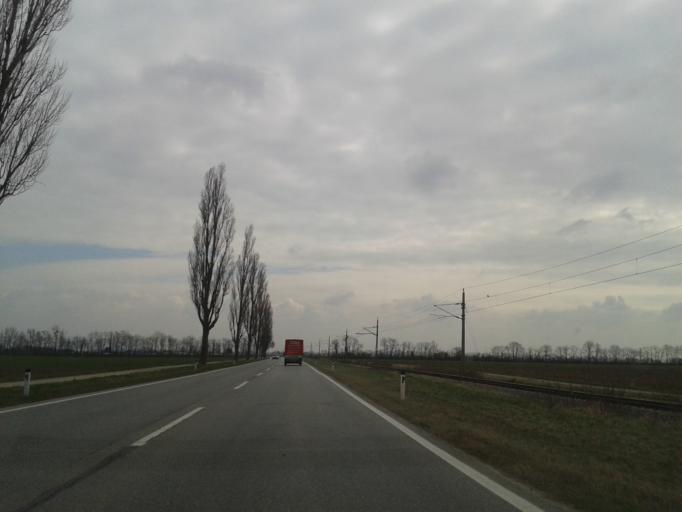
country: AT
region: Lower Austria
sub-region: Politischer Bezirk Bruck an der Leitha
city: Scharndorf
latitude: 48.1076
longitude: 16.7505
